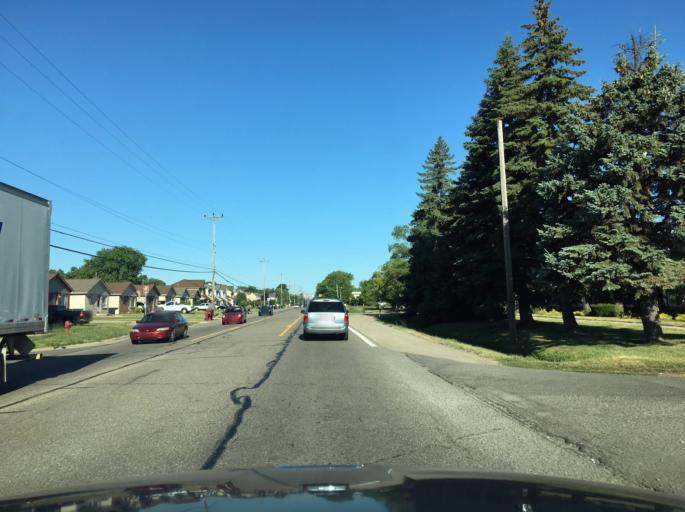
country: US
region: Michigan
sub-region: Macomb County
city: Fraser
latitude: 42.5396
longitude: -82.9163
